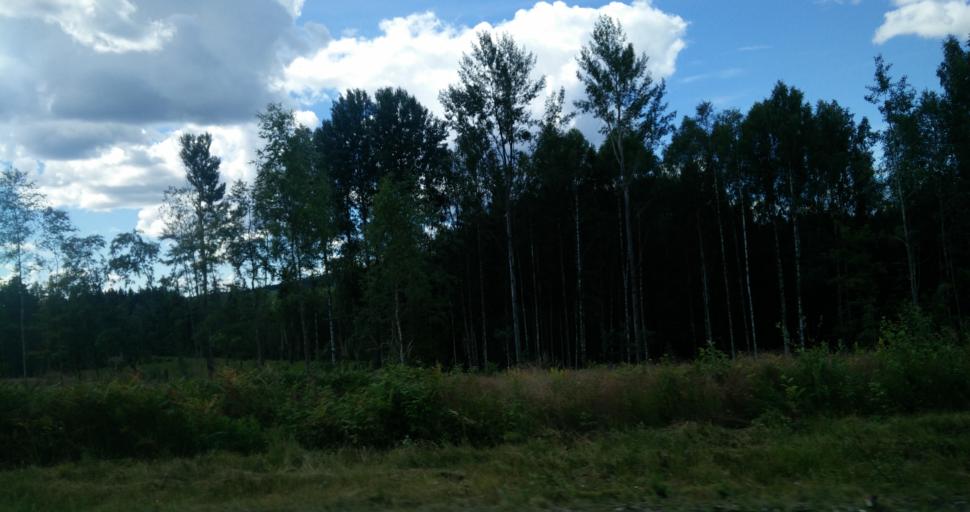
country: SE
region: Vaermland
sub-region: Hagfors Kommun
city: Ekshaerad
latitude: 60.0415
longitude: 13.5334
